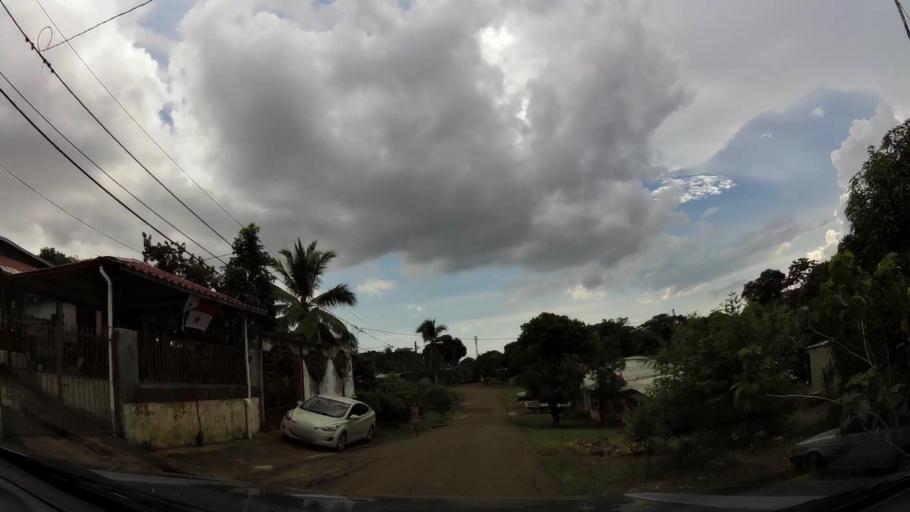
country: PA
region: Panama
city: Cabra Numero Uno
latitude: 9.1051
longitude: -79.3205
